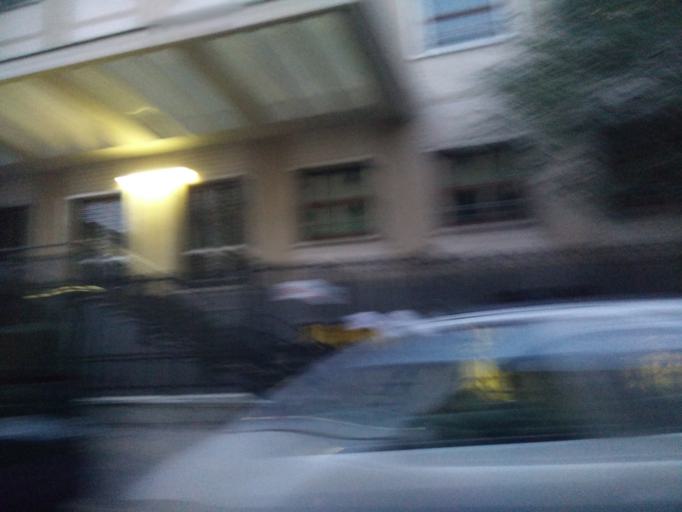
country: IT
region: Piedmont
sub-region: Provincia di Torino
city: Lesna
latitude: 45.0443
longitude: 7.6453
